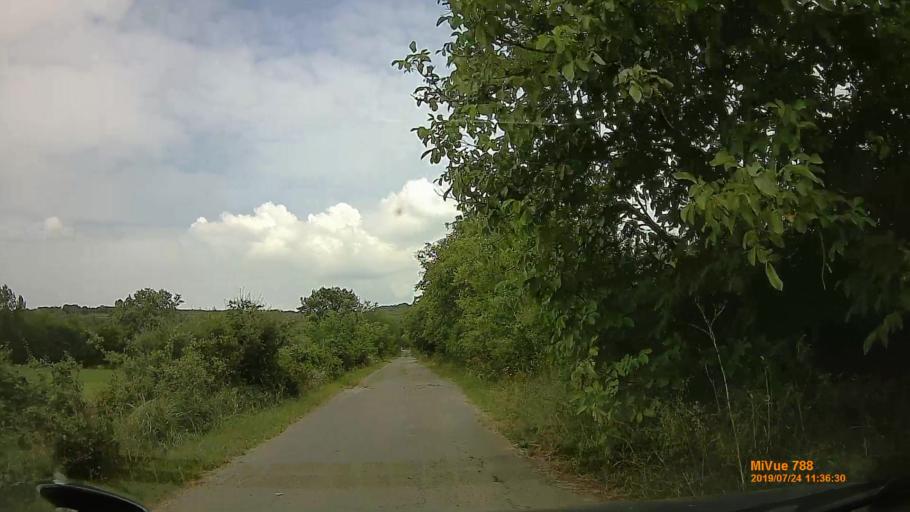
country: UA
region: Zakarpattia
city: Batiovo
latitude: 48.2391
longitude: 22.4774
